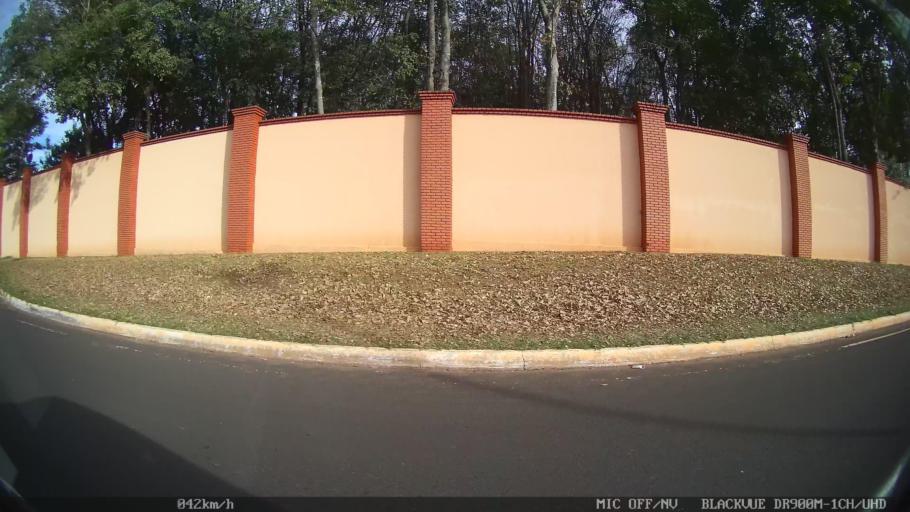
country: BR
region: Sao Paulo
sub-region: Catanduva
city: Catanduva
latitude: -21.1122
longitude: -48.9627
